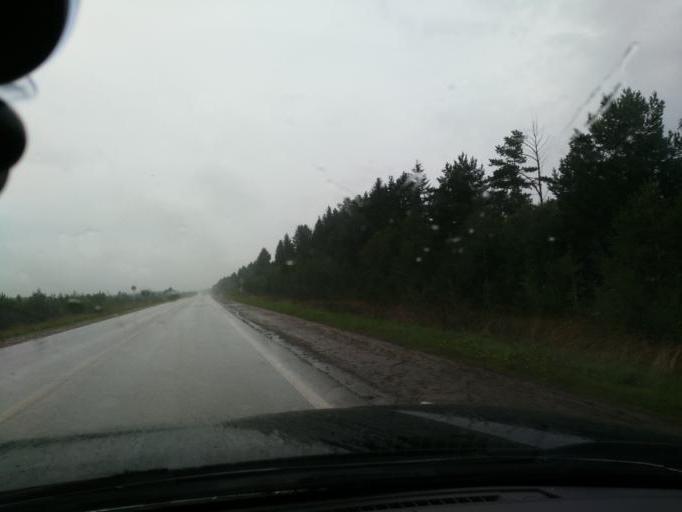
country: RU
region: Perm
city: Osa
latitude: 57.3363
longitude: 55.5849
